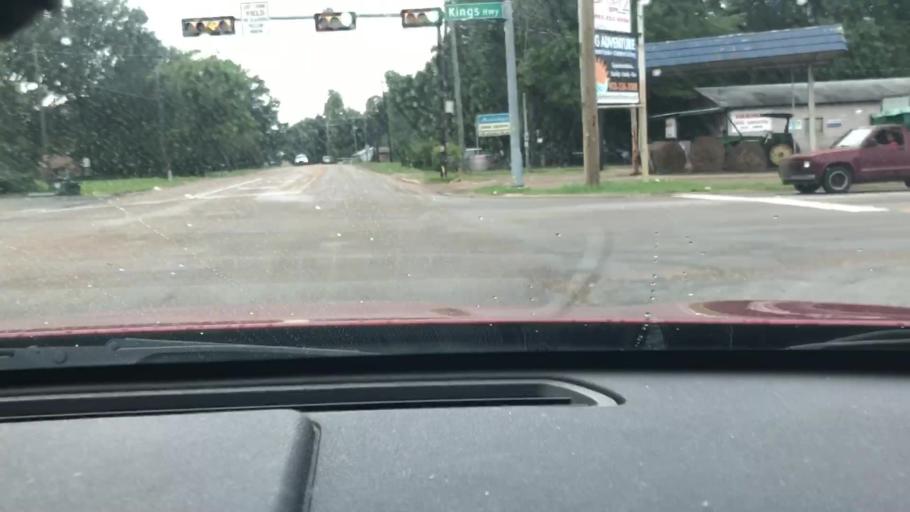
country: US
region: Texas
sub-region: Bowie County
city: Nash
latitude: 33.4425
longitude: -94.1306
